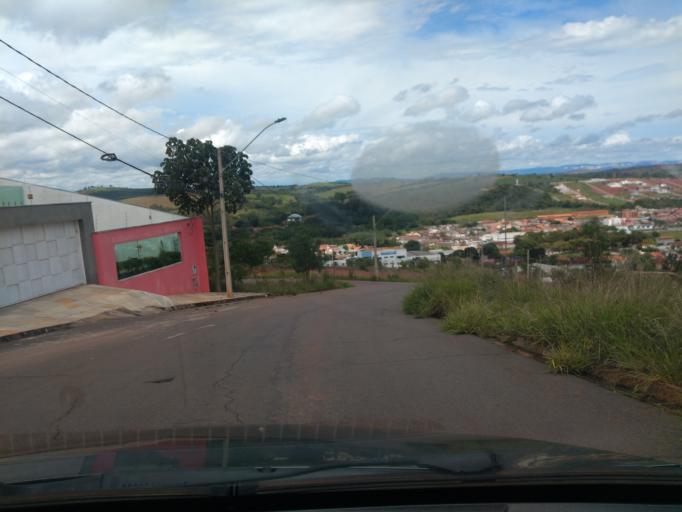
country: BR
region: Minas Gerais
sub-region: Tres Coracoes
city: Tres Coracoes
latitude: -21.6708
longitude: -45.2757
